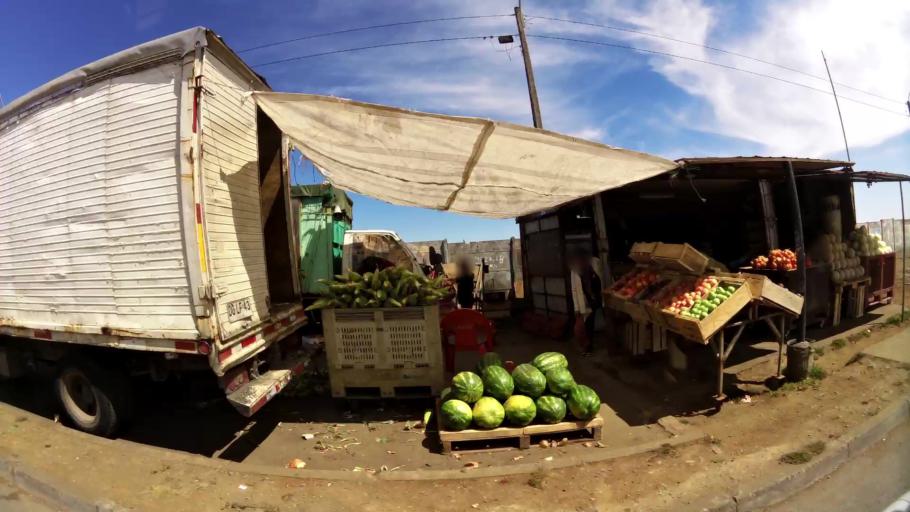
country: CL
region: Biobio
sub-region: Provincia de Concepcion
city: Talcahuano
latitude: -36.7090
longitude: -73.1294
